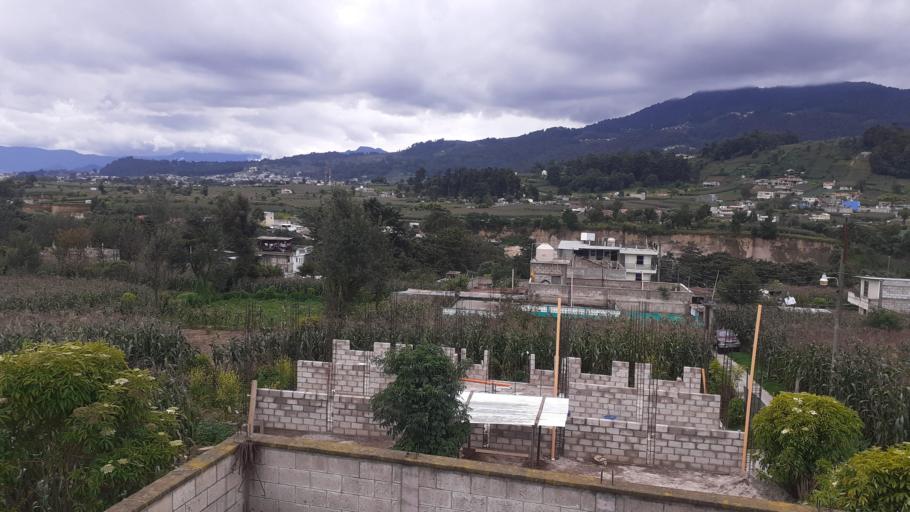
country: GT
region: Quetzaltenango
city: Ostuncalco
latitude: 14.8709
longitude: -91.6115
